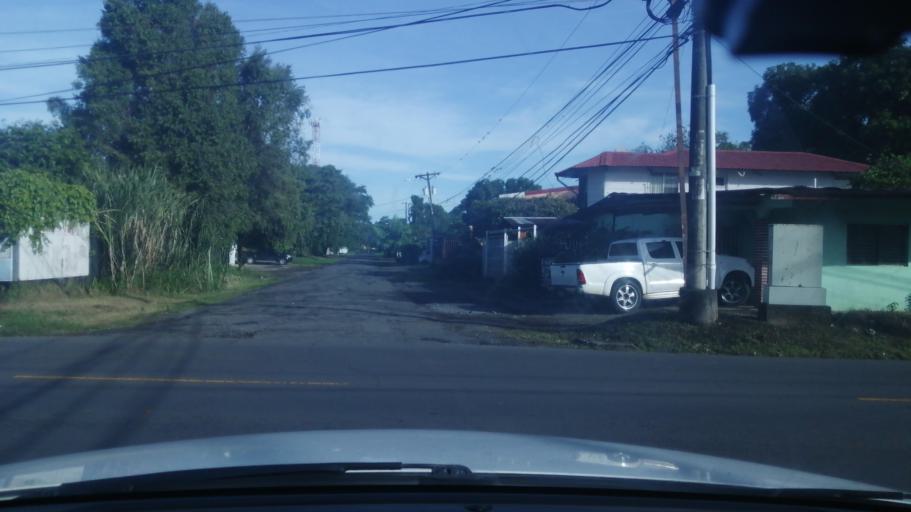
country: PA
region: Chiriqui
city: David
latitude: 8.4428
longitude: -82.4283
